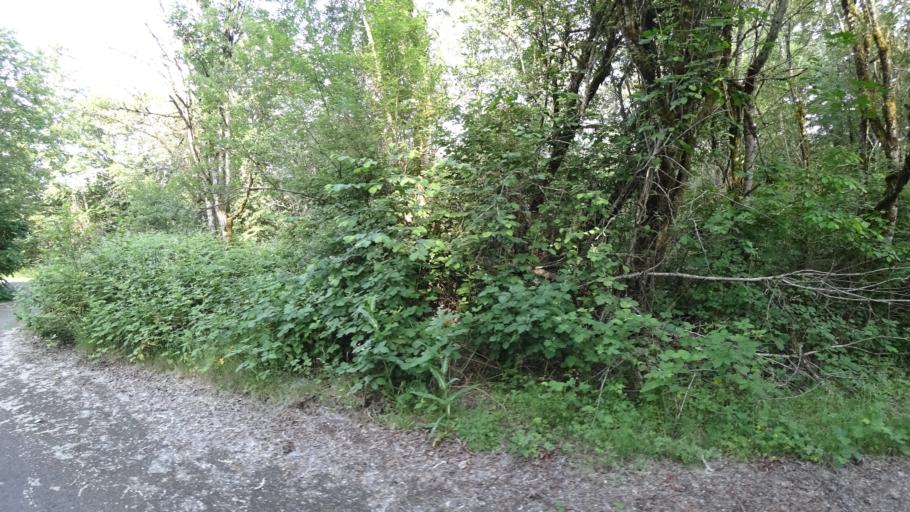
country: US
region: Oregon
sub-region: Clackamas County
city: Happy Valley
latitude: 45.4492
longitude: -122.5018
